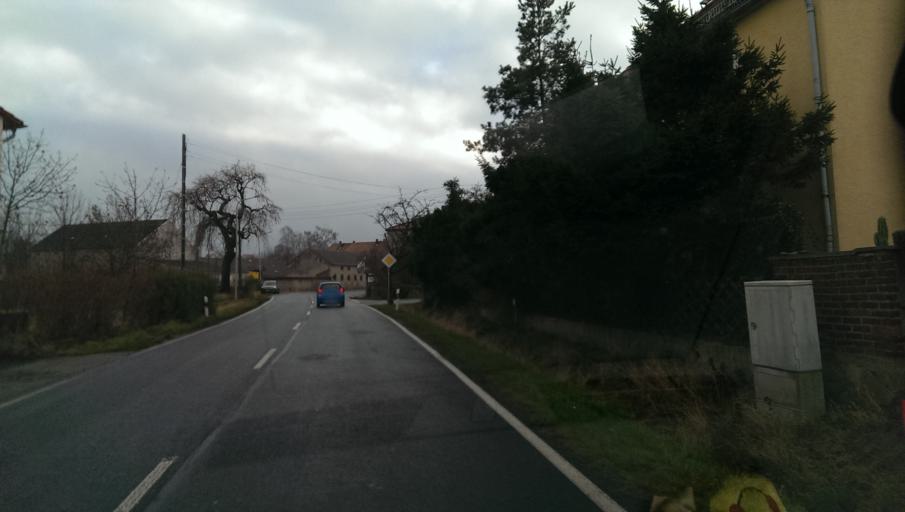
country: DE
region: Saxony
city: Niederau
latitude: 51.2193
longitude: 13.5677
